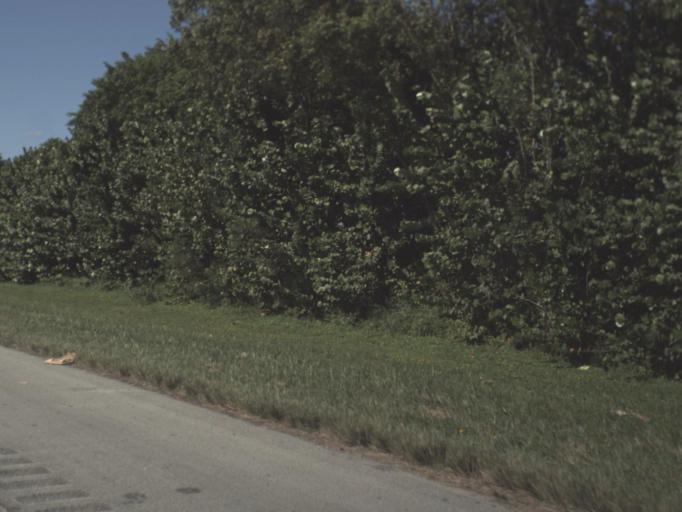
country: US
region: Florida
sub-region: Miami-Dade County
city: Princeton
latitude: 25.5229
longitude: -80.4008
